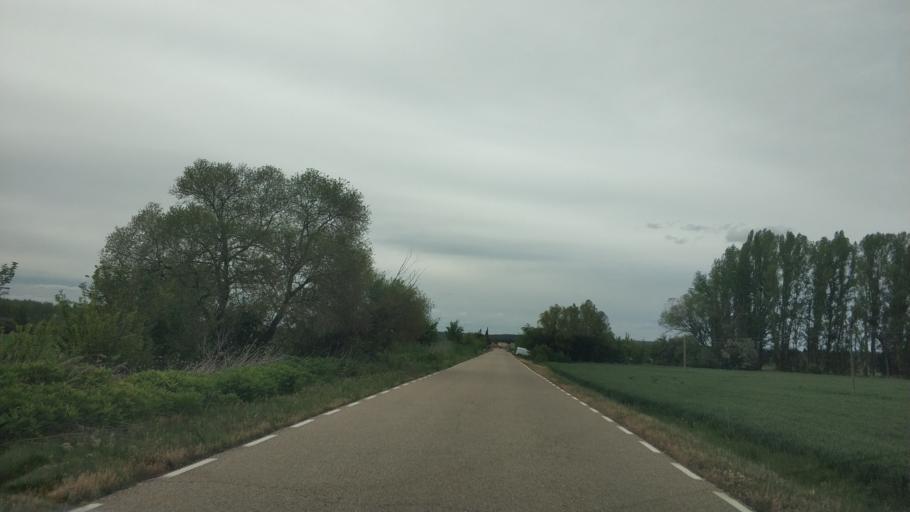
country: ES
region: Castille and Leon
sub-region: Provincia de Soria
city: Berlanga de Duero
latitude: 41.4907
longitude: -2.8676
